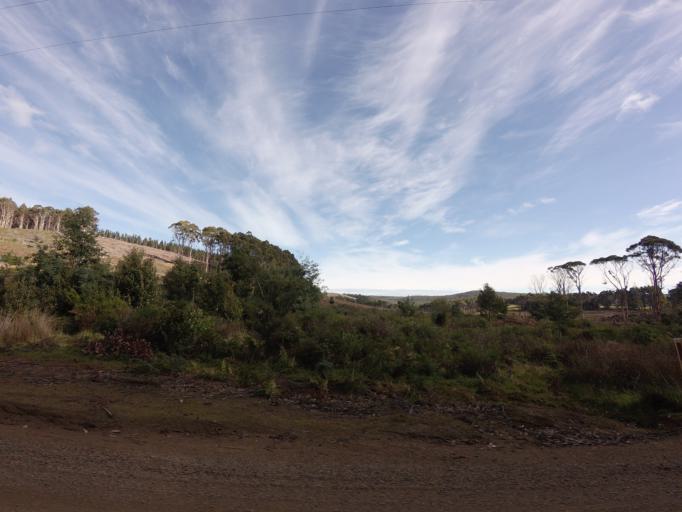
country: AU
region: Tasmania
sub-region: Clarence
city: Sandford
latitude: -43.1728
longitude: 147.7702
